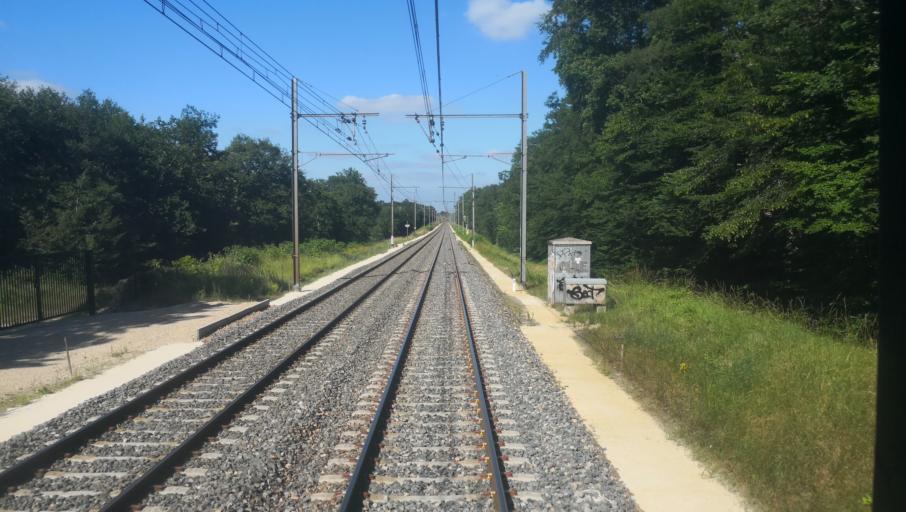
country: FR
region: Ile-de-France
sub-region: Departement de Seine-et-Marne
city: Veneux-les-Sablons
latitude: 48.3566
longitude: 2.7937
